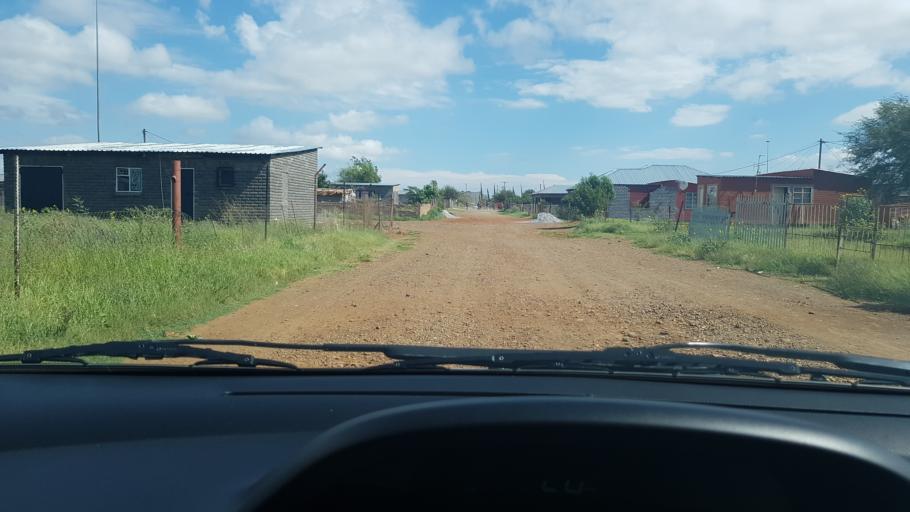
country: ZA
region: Northern Cape
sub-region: Siyanda District Municipality
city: Danielskuil
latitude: -28.1916
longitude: 23.5419
